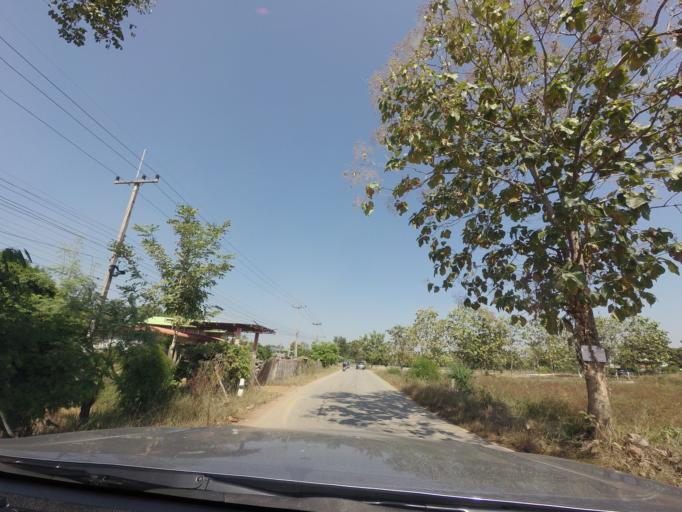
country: TH
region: Sukhothai
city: Si Samrong
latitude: 17.2016
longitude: 99.7736
